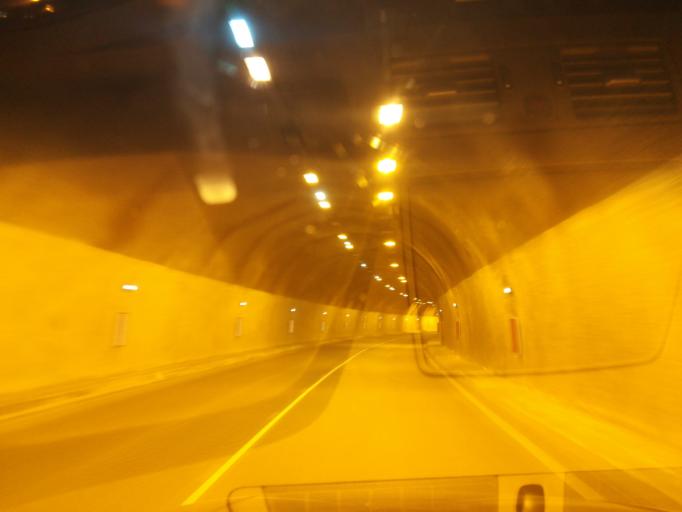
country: BG
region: Plovdiv
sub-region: Obshtina Asenovgrad
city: Asenovgrad
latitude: 41.9619
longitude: 24.8615
